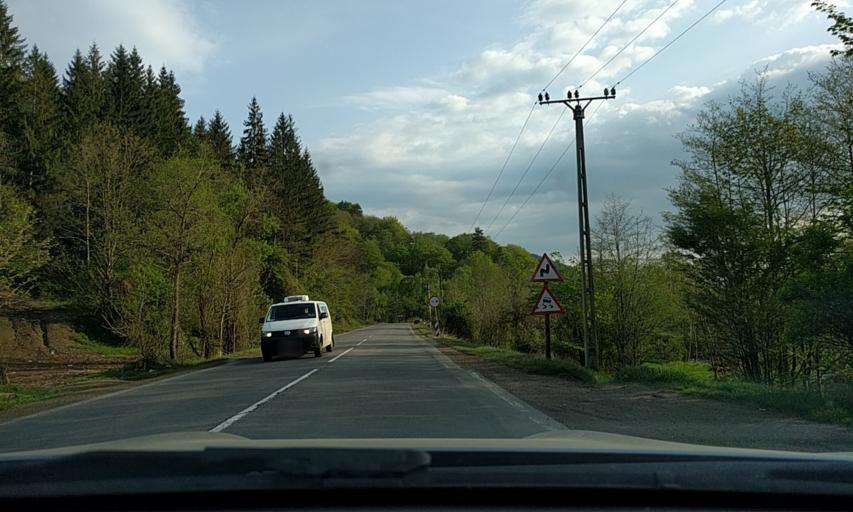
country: RO
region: Bacau
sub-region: Oras Slanic-Moldova
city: Slanic-Moldova
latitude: 46.1246
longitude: 26.4371
